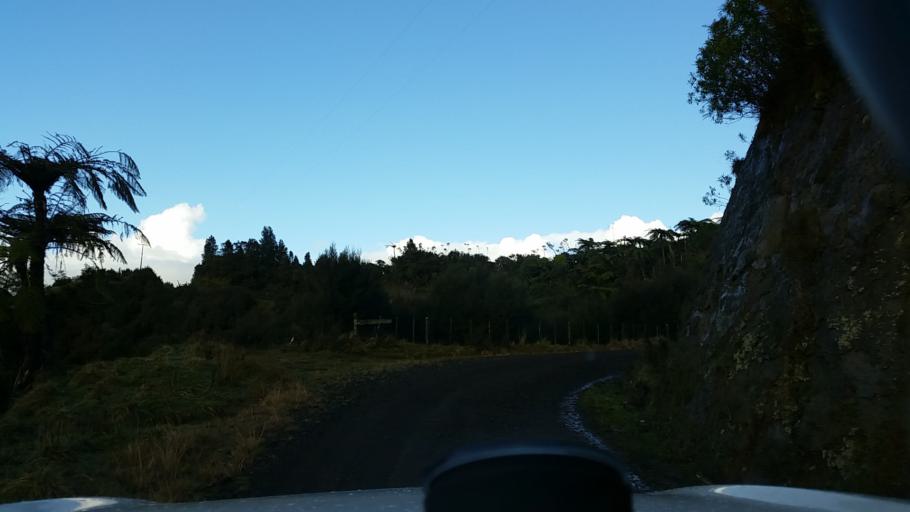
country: NZ
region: Taranaki
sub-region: South Taranaki District
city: Eltham
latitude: -39.4181
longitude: 174.5569
